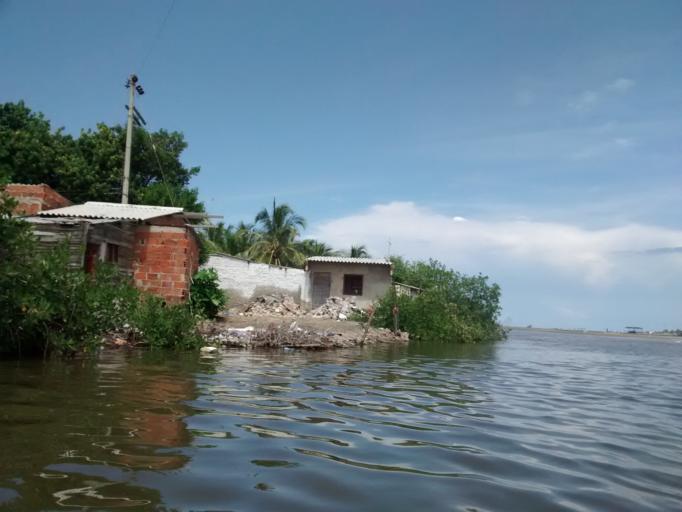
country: CO
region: Bolivar
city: Cartagena
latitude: 10.4864
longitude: -75.4891
